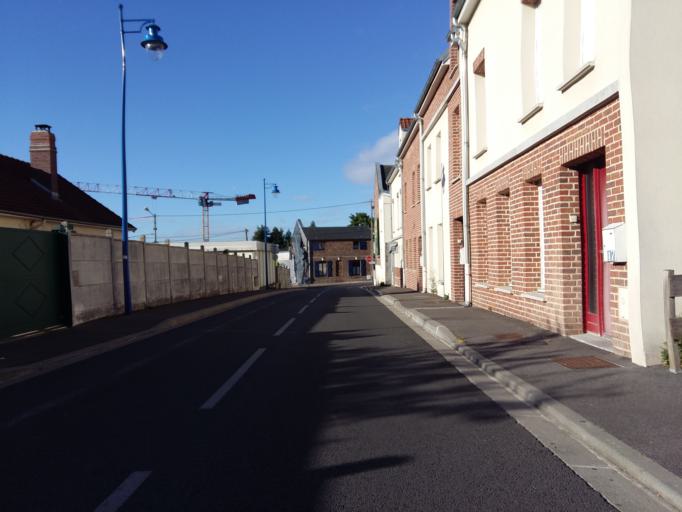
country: FR
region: Picardie
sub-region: Departement de la Somme
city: Rivery
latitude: 49.9027
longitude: 2.3252
